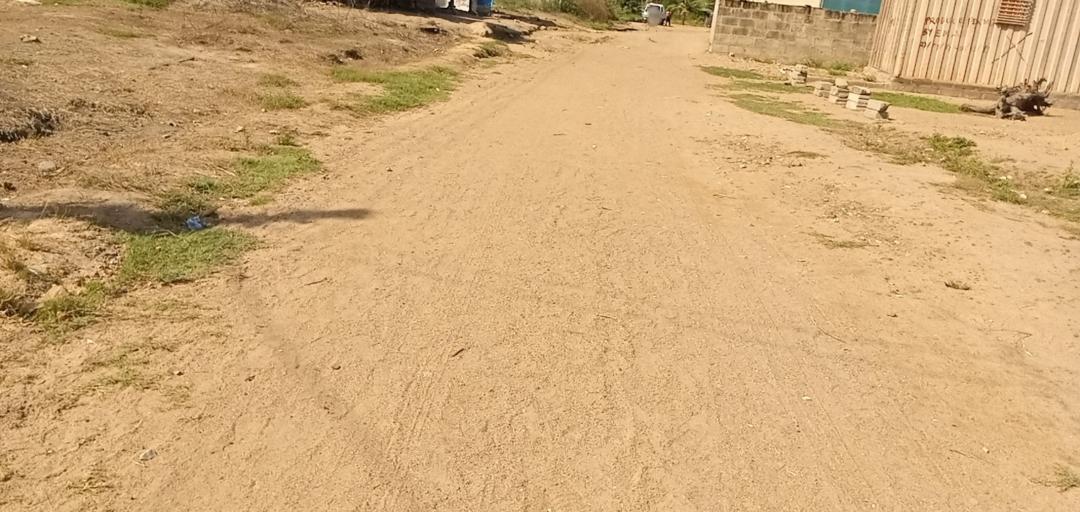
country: GH
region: Central
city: Winneba
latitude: 5.3530
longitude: -0.6231
